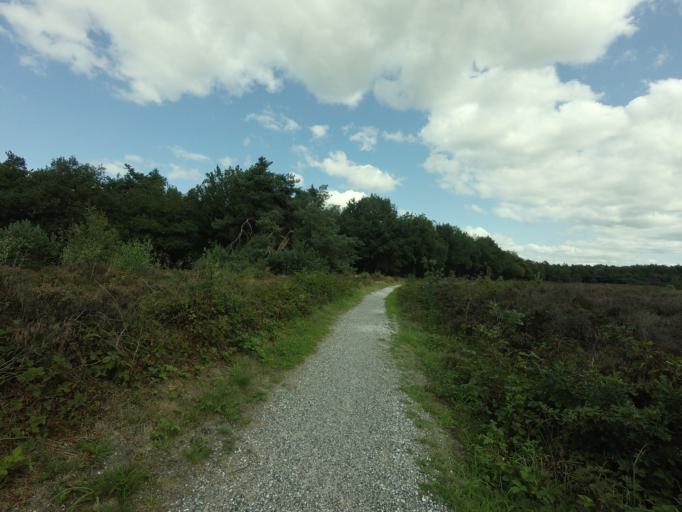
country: NL
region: Overijssel
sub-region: Gemeente Staphorst
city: Staphorst
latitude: 52.6336
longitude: 6.2755
